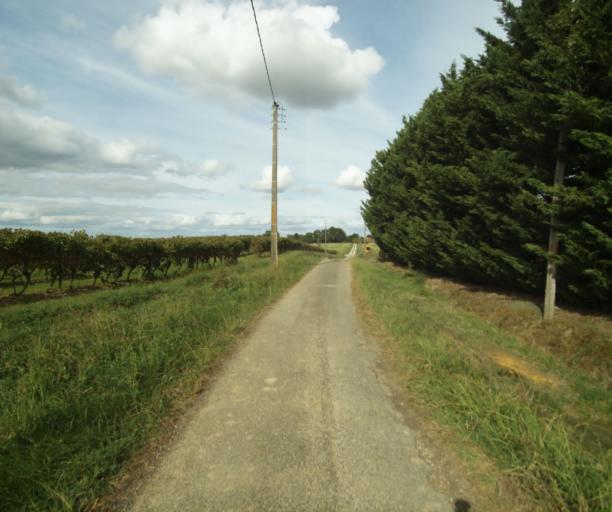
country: FR
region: Midi-Pyrenees
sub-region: Departement du Gers
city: Eauze
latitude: 43.8558
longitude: 0.1527
